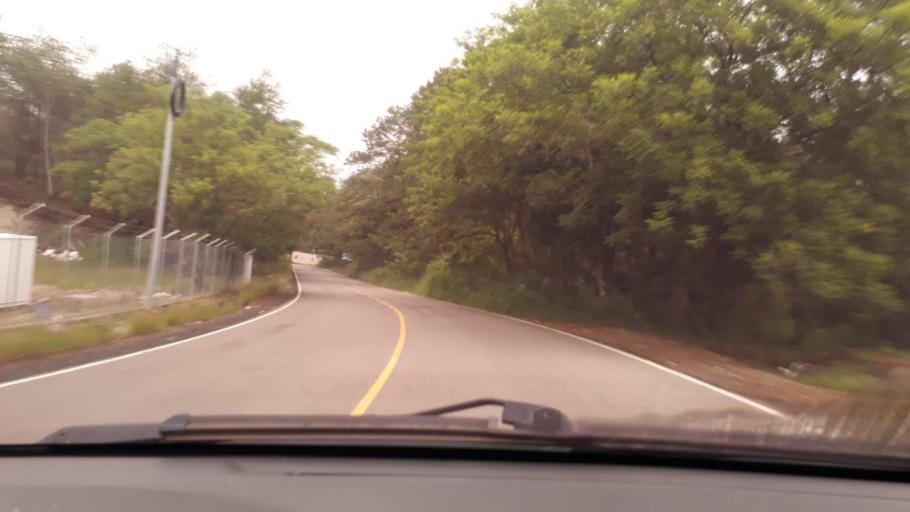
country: GT
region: Chiquimula
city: Esquipulas
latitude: 14.5476
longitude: -89.2858
